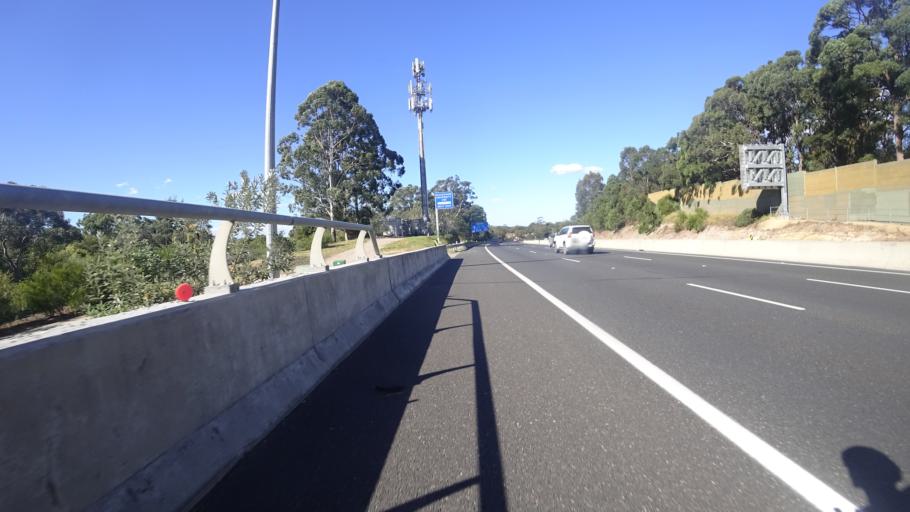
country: AU
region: New South Wales
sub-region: Ryde
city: Macquarie Park
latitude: -33.7643
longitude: 151.1061
